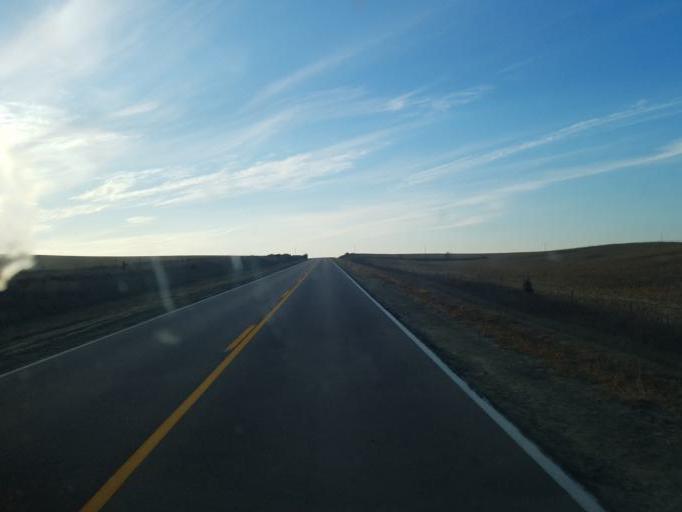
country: US
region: Nebraska
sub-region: Cedar County
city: Hartington
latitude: 42.7286
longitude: -97.3430
